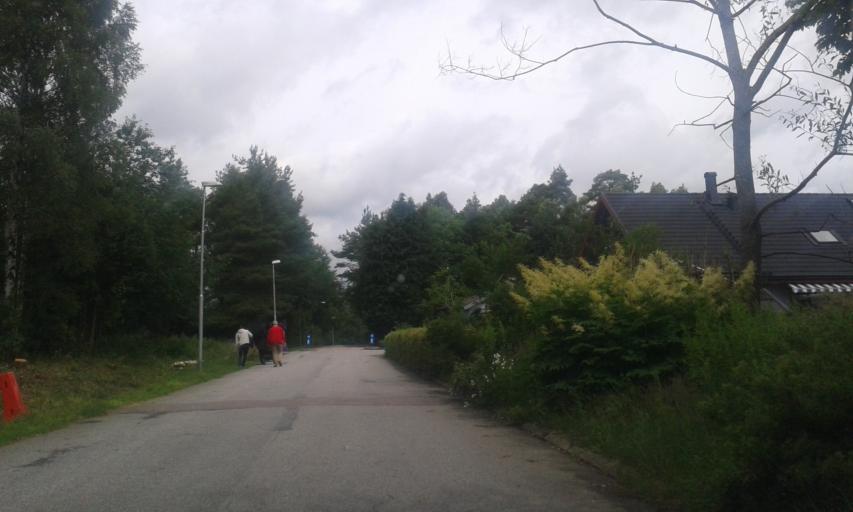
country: SE
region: Vaestra Goetaland
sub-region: Kungalvs Kommun
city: Kungalv
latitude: 57.8671
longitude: 11.9085
